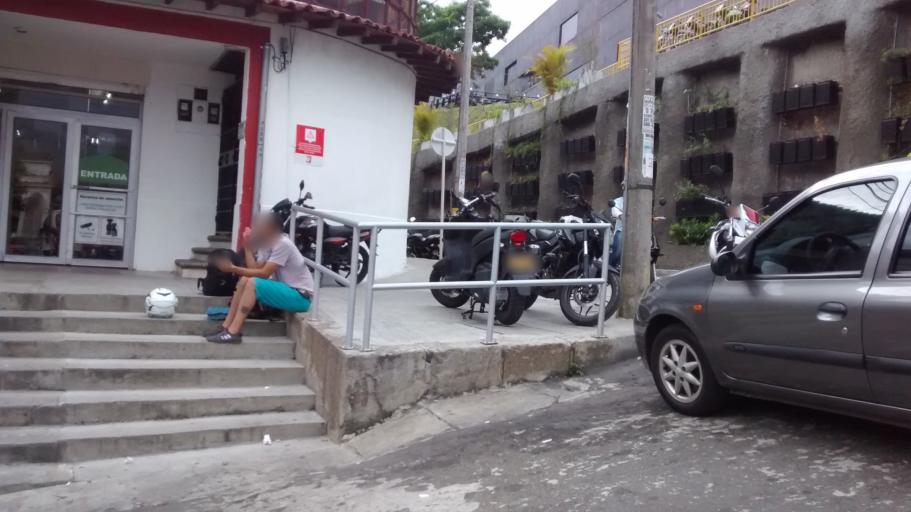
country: CO
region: Antioquia
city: Medellin
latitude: 6.2777
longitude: -75.6361
